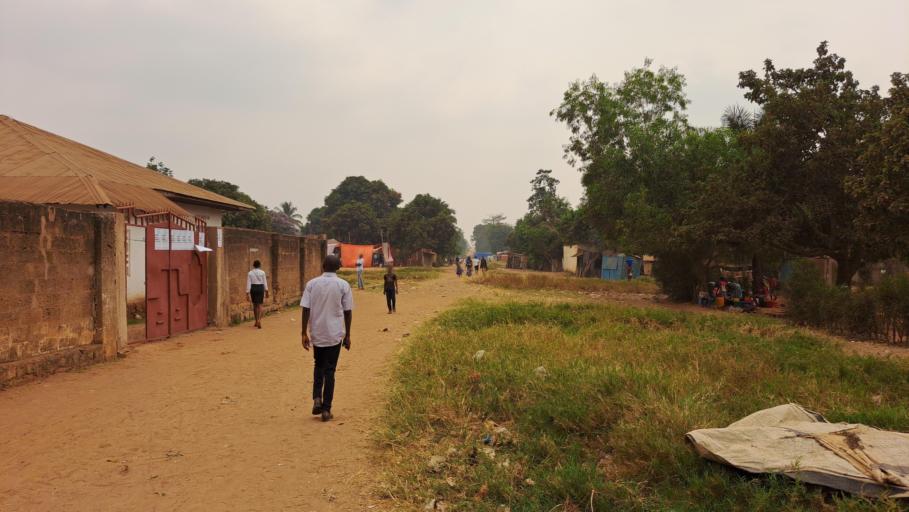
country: CD
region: Kasai-Oriental
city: Mbuji-Mayi
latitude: -6.1170
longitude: 23.6008
